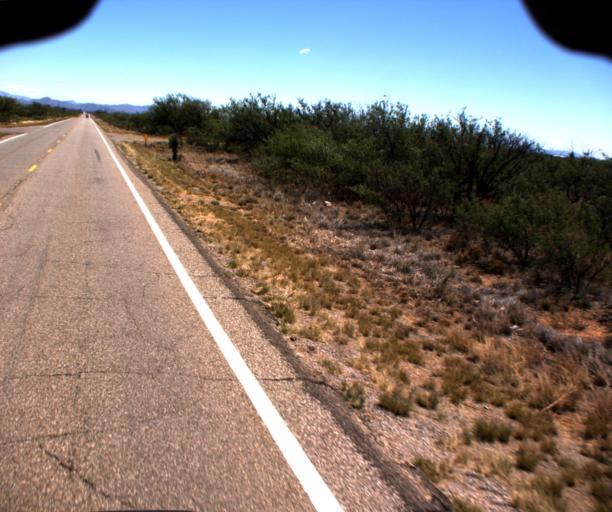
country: US
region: Arizona
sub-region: Cochise County
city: Huachuca City
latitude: 31.6924
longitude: -110.3681
